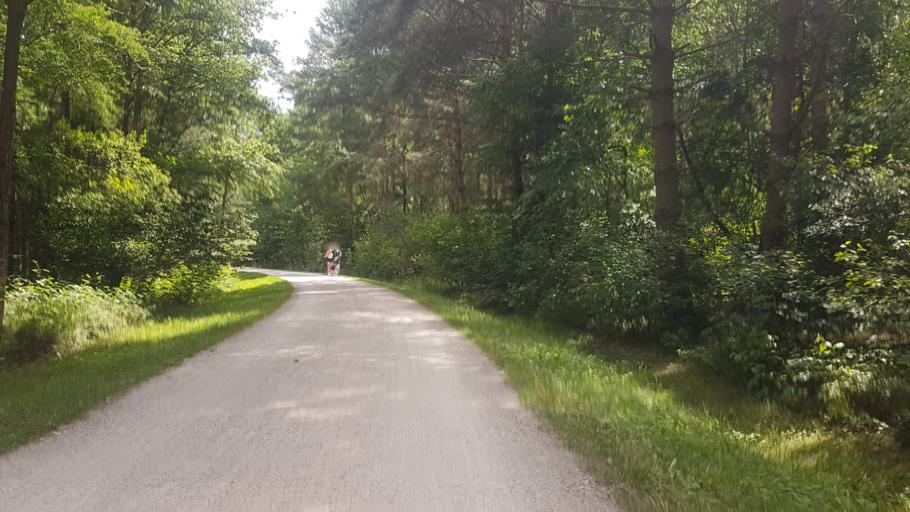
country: DE
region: Bavaria
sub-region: Regierungsbezirk Mittelfranken
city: Absberg
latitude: 49.1281
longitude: 10.8825
